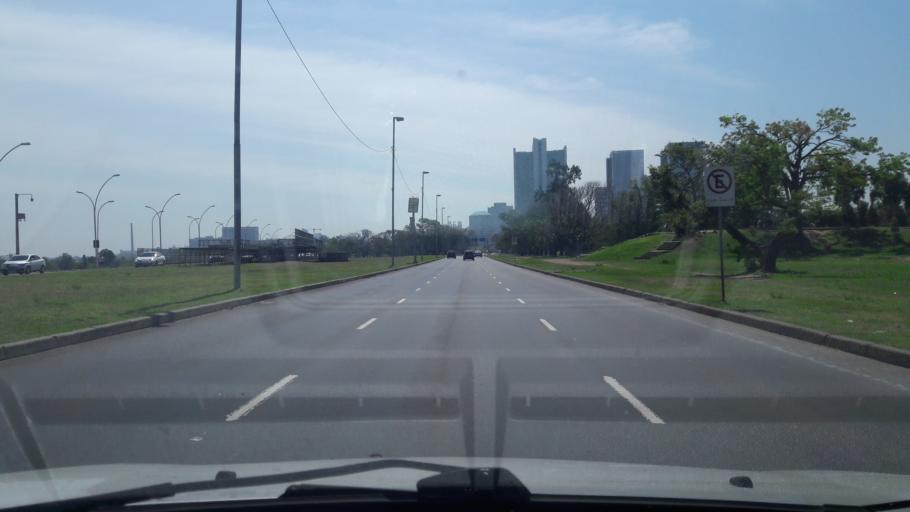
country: BR
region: Rio Grande do Sul
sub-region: Porto Alegre
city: Porto Alegre
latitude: -30.0520
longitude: -51.2319
